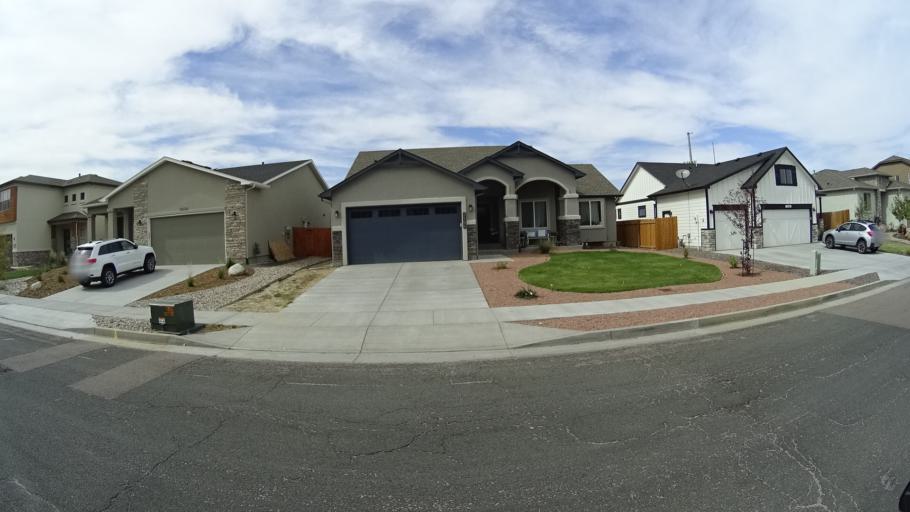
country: US
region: Colorado
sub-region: El Paso County
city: Cimarron Hills
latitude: 38.9041
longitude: -104.7010
